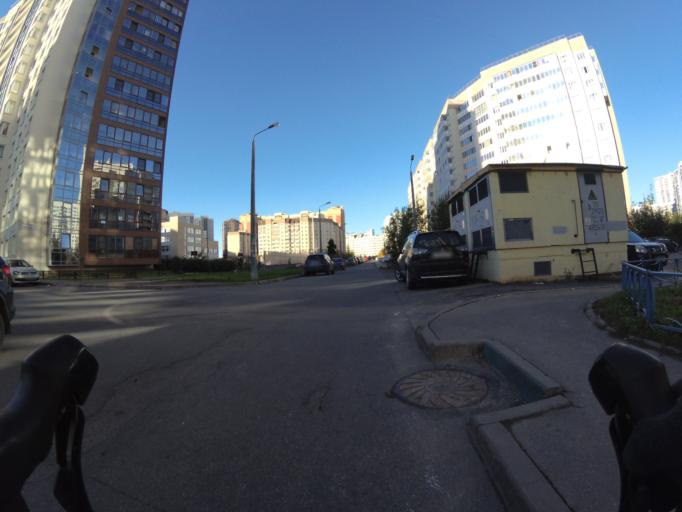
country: RU
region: Leningrad
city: Untolovo
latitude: 60.0001
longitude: 30.2066
